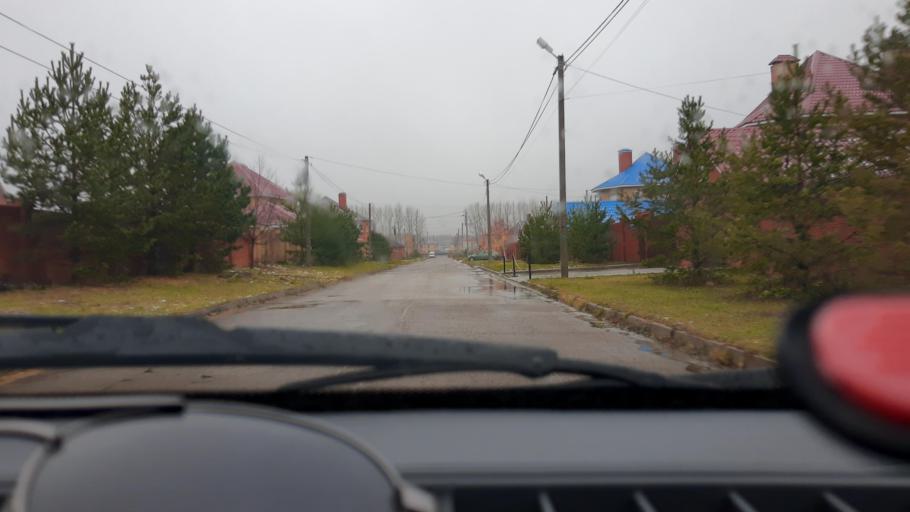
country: RU
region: Bashkortostan
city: Kabakovo
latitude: 54.6216
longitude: 56.1227
